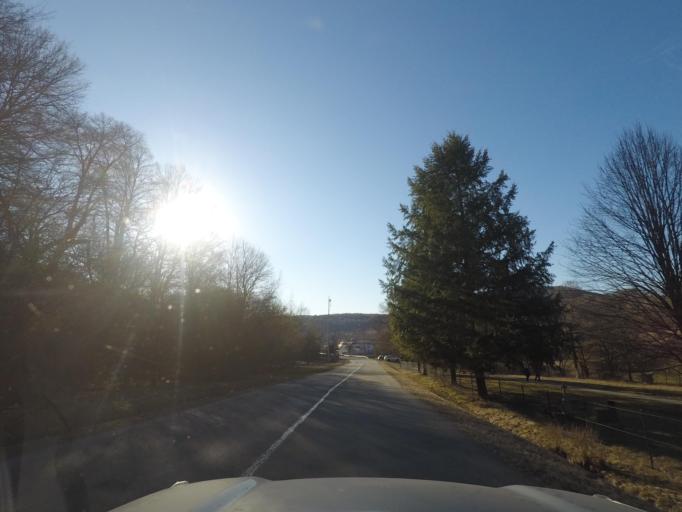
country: SK
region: Presovsky
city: Medzilaborce
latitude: 49.2808
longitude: 21.8274
